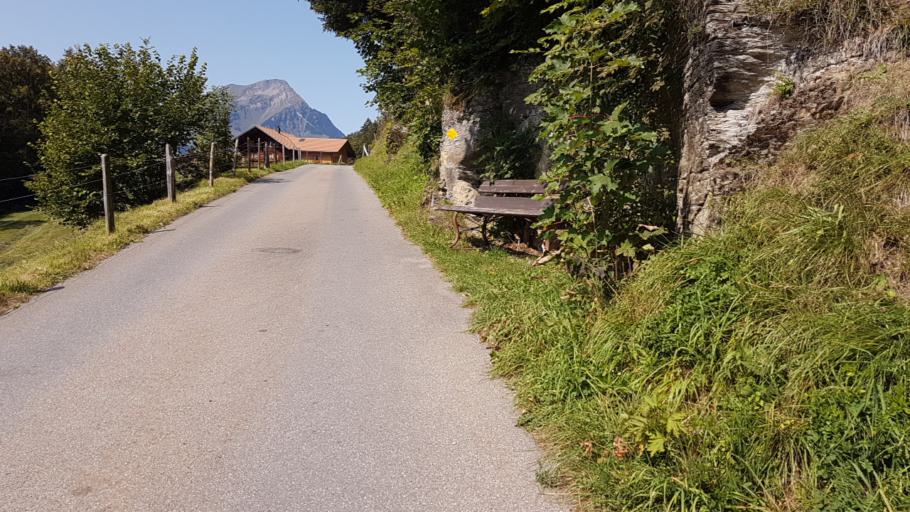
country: CH
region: Bern
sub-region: Frutigen-Niedersimmental District
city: Aeschi
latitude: 46.5960
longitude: 7.7161
